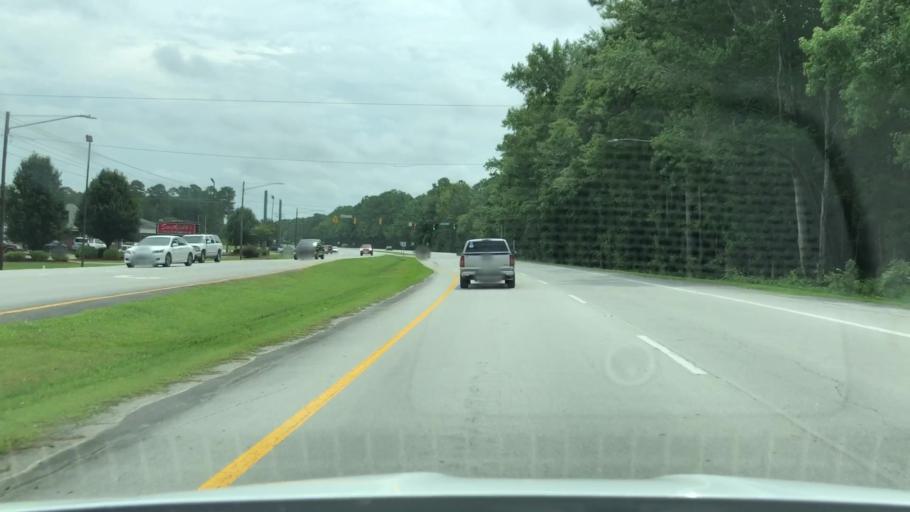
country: US
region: North Carolina
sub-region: Craven County
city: Havelock
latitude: 34.8569
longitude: -76.8960
